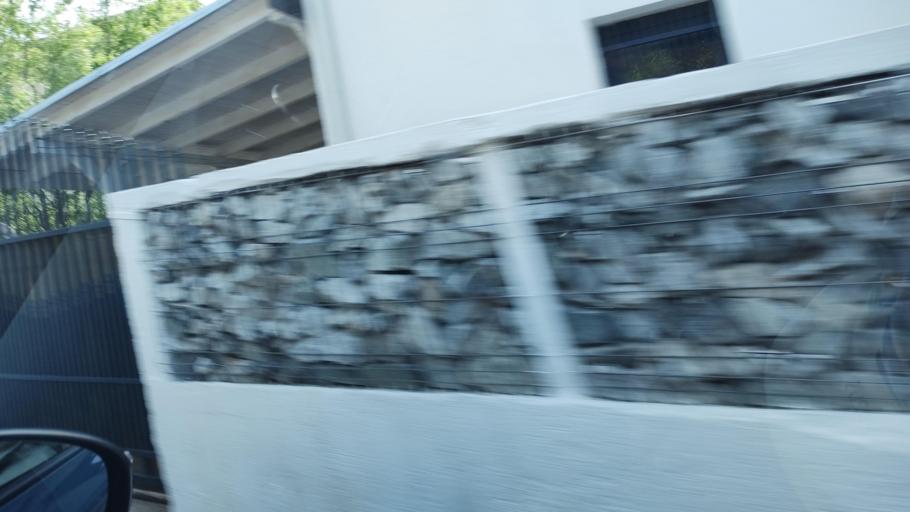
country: RO
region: Mehedinti
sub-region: Comuna Eselnita
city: Eselnita
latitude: 44.6841
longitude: 22.3605
